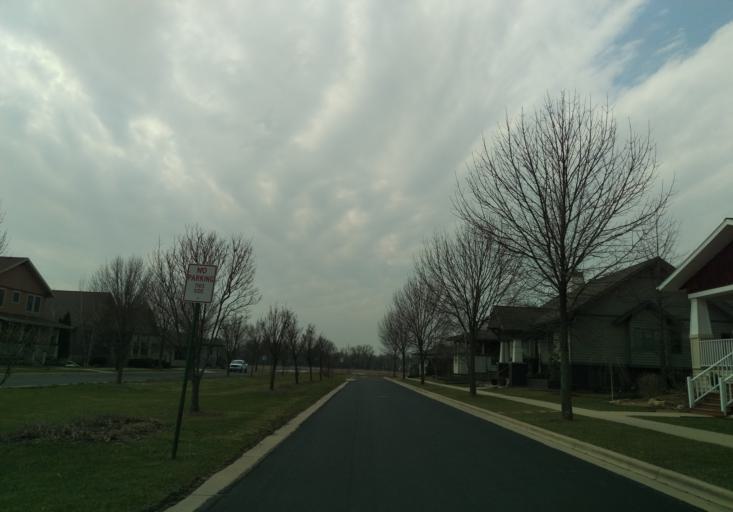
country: US
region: Wisconsin
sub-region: Dane County
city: Middleton
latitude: 43.1129
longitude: -89.4963
